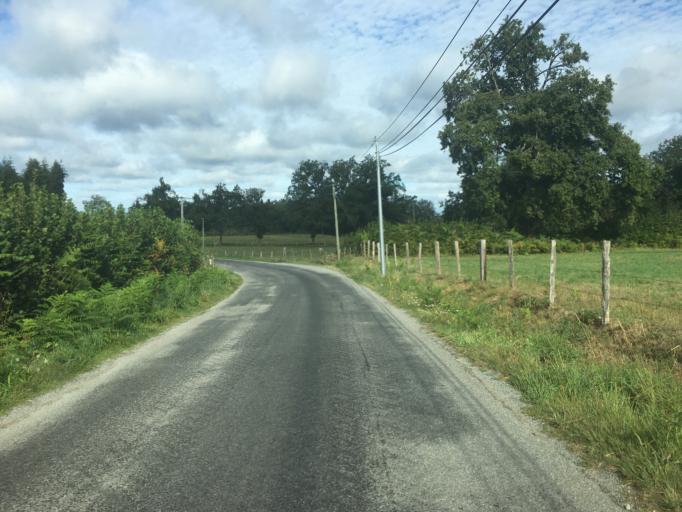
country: FR
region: Auvergne
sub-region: Departement du Cantal
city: Champagnac
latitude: 45.4152
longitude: 2.4223
